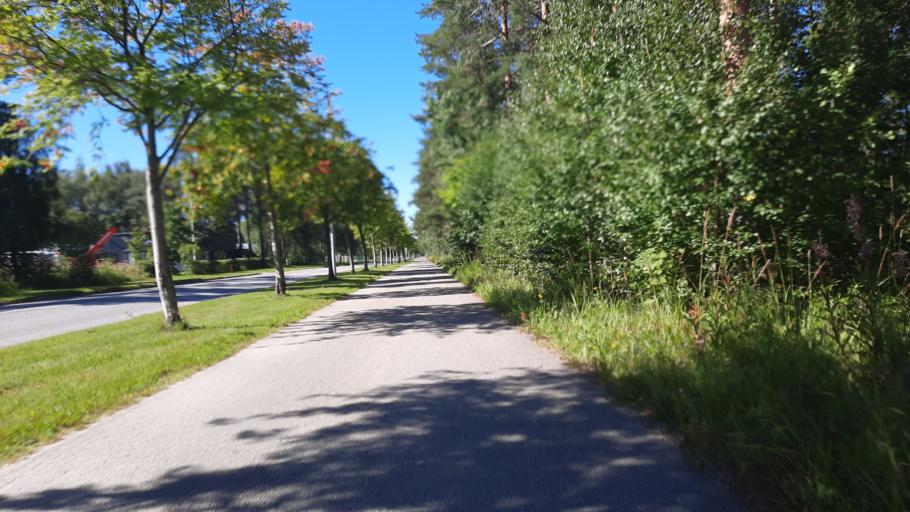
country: FI
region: North Karelia
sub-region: Joensuu
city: Joensuu
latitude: 62.6217
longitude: 29.7524
